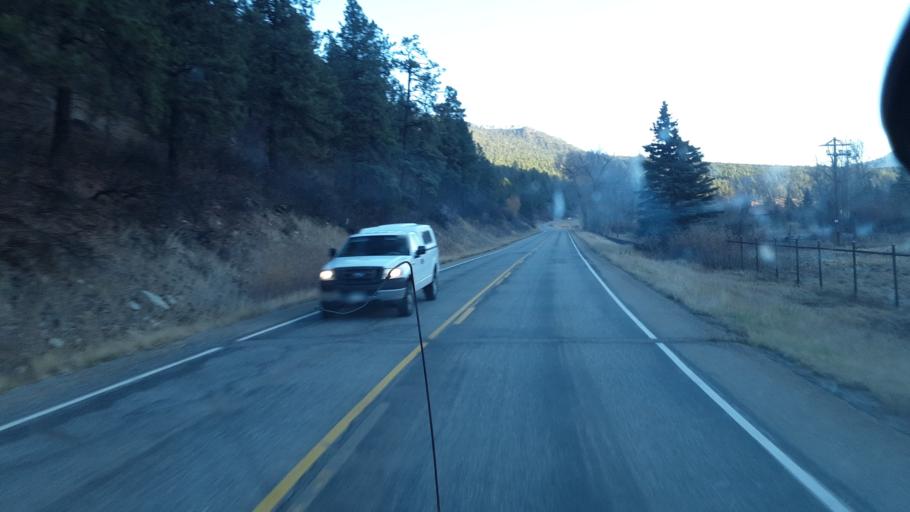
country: US
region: Colorado
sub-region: La Plata County
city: Durango
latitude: 37.3379
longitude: -107.7242
